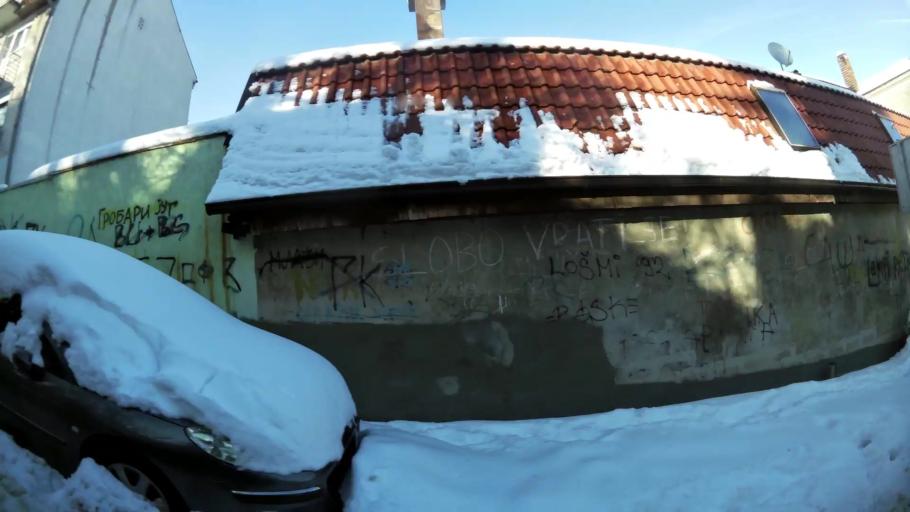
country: RS
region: Central Serbia
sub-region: Belgrade
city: Palilula
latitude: 44.8161
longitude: 20.4988
